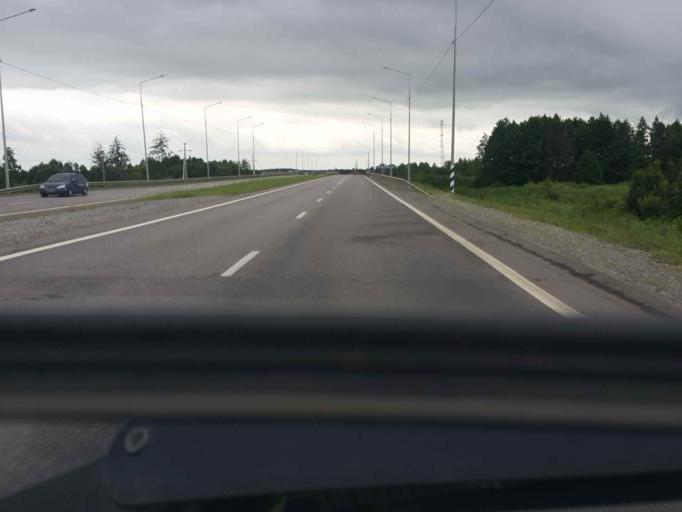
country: RU
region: Tambov
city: Zavoronezhskoye
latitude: 52.8667
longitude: 40.7613
